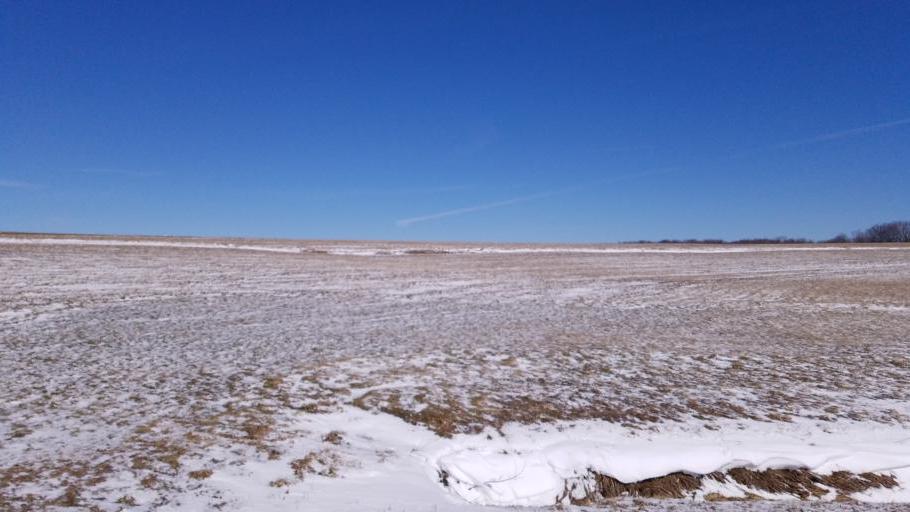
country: US
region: New York
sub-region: Allegany County
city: Andover
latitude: 42.0608
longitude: -77.8003
